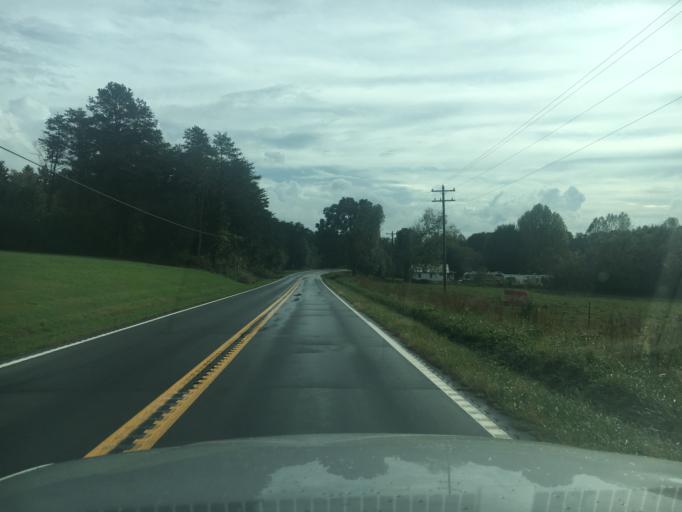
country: US
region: North Carolina
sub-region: Rutherford County
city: Spindale
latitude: 35.4429
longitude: -81.8909
